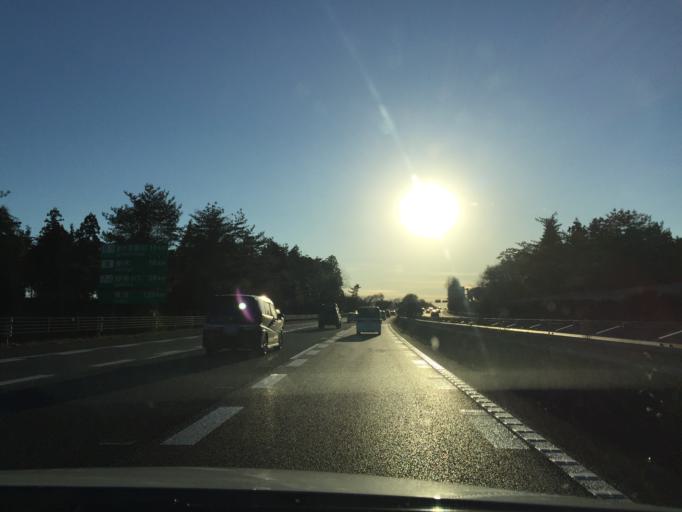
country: JP
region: Tochigi
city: Kanuma
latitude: 36.5319
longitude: 139.7937
